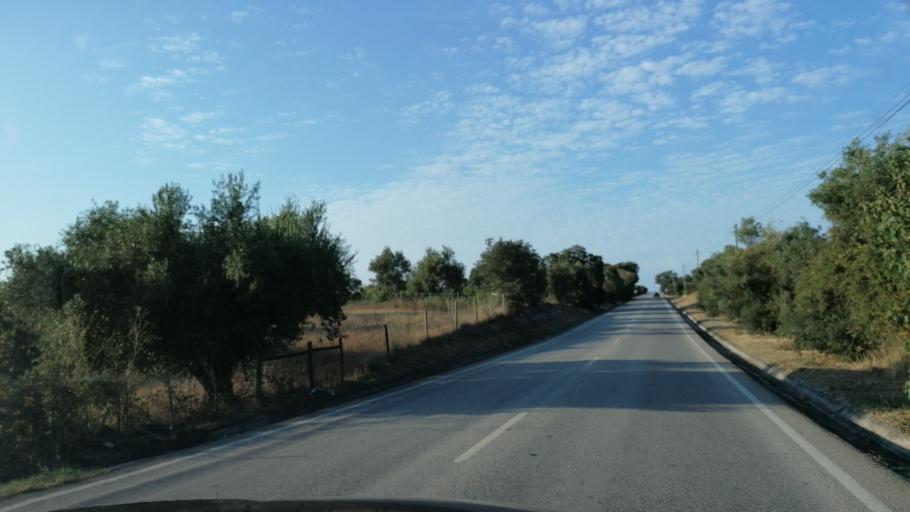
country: PT
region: Santarem
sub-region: Alcanena
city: Alcanena
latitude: 39.4208
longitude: -8.6357
